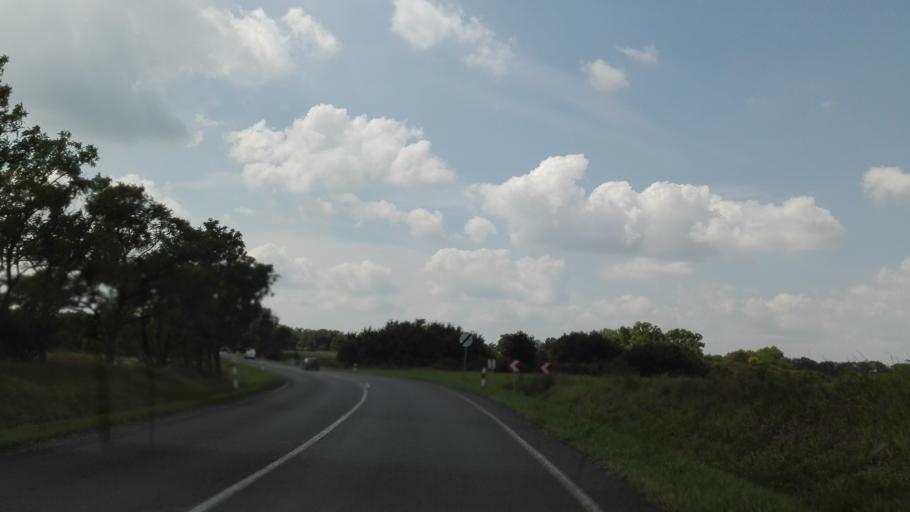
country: HU
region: Fejer
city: Alap
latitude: 46.8000
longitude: 18.7205
